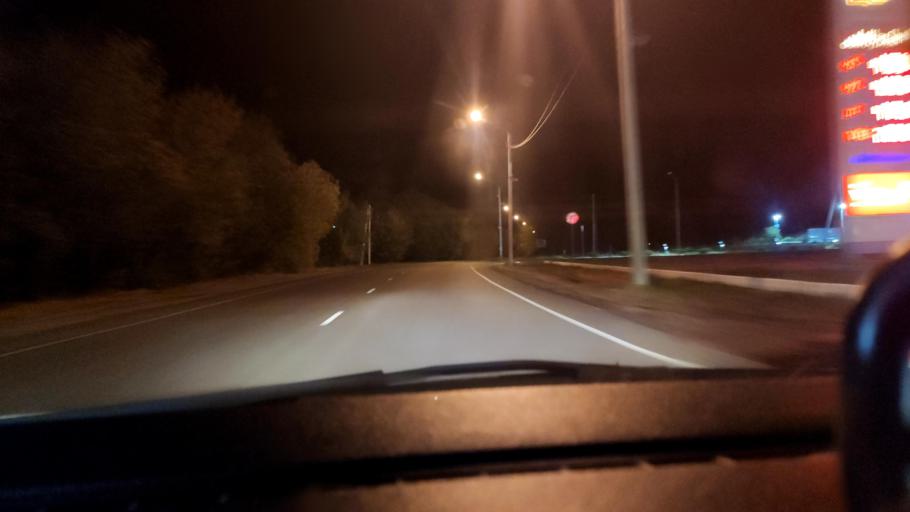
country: RU
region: Voronezj
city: Voronezh
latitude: 51.6155
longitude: 39.1785
